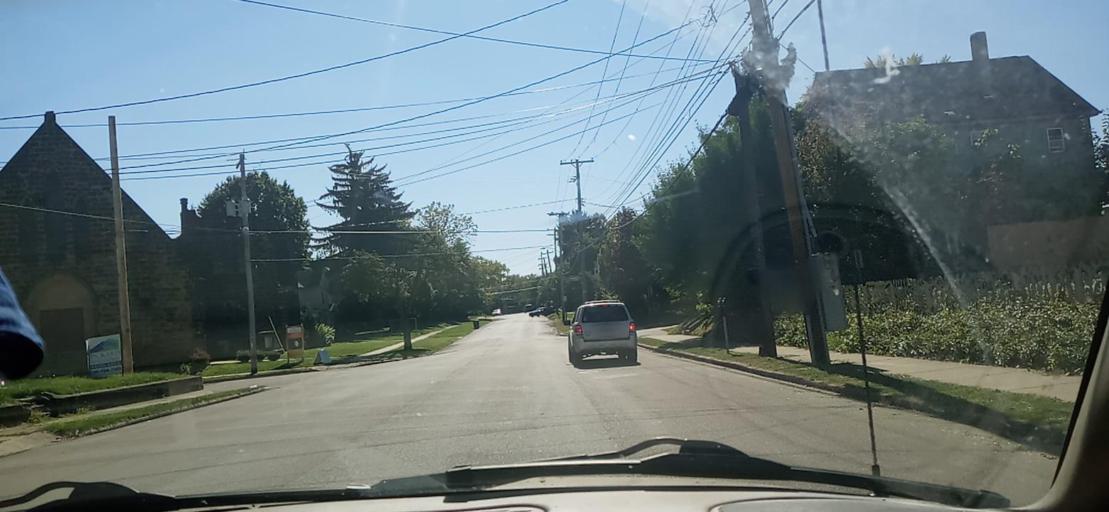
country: US
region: Ohio
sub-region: Summit County
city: Akron
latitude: 41.0705
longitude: -81.5069
